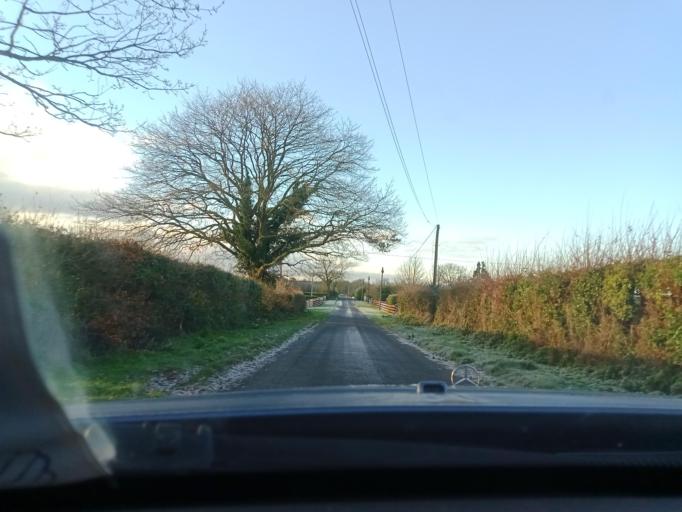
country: IE
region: Leinster
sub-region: County Carlow
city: Bagenalstown
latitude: 52.6481
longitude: -7.0012
